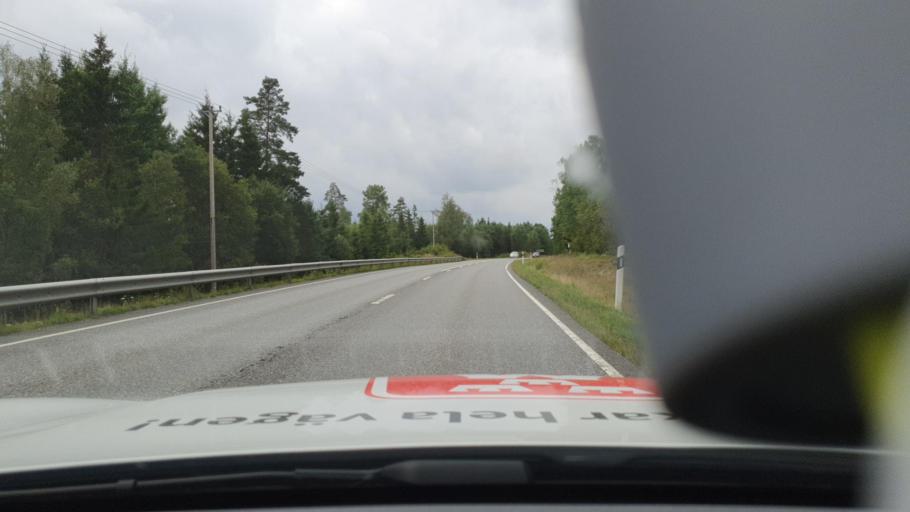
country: SE
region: Joenkoeping
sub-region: Gislaveds Kommun
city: Smalandsstenar
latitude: 57.1862
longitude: 13.4346
